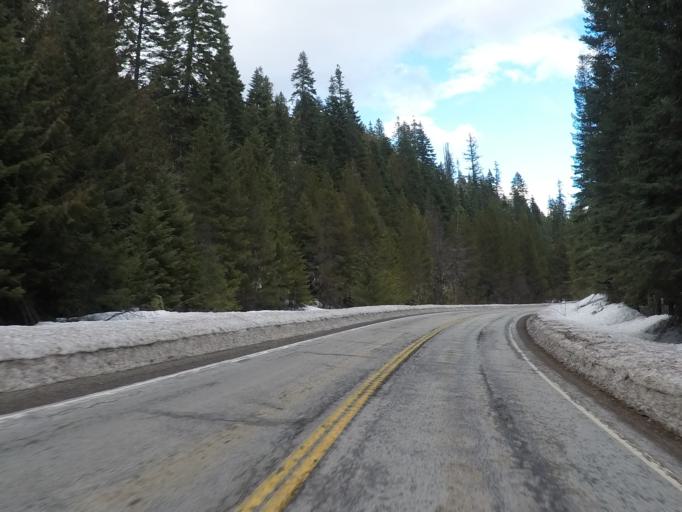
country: US
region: Montana
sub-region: Mineral County
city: Superior
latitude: 46.4865
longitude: -114.8789
